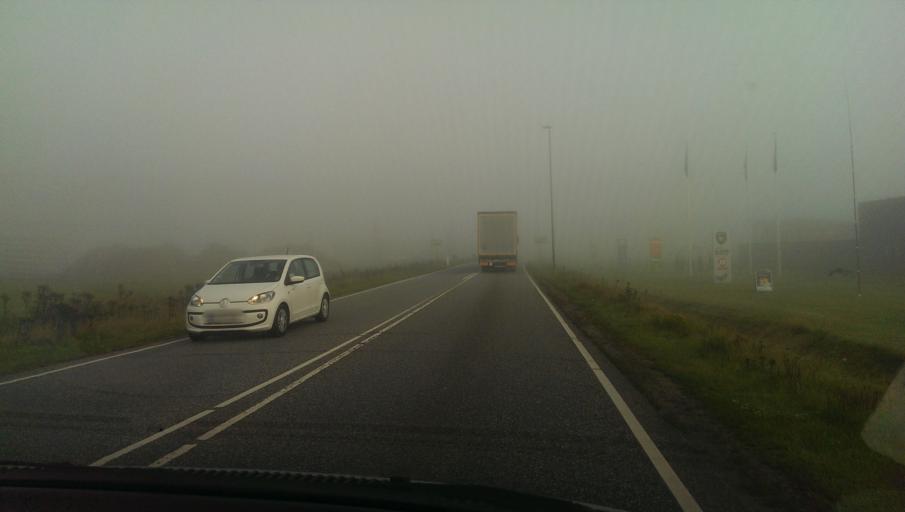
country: DK
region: South Denmark
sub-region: Vejen Kommune
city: Vejen
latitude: 55.4905
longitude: 9.1308
